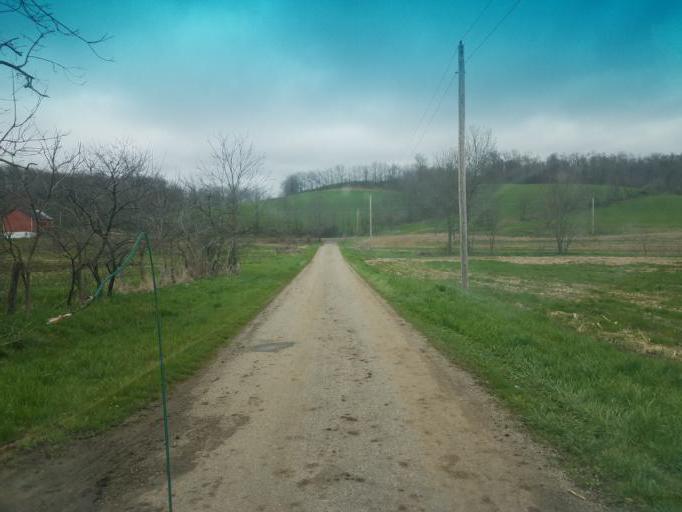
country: US
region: Ohio
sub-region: Stark County
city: Beach City
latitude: 40.6117
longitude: -81.6610
